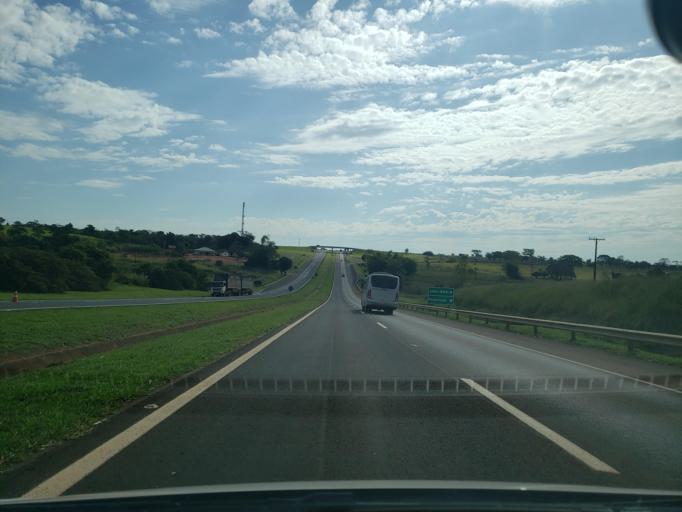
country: BR
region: Sao Paulo
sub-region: Promissao
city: Promissao
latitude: -21.6030
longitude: -49.8805
